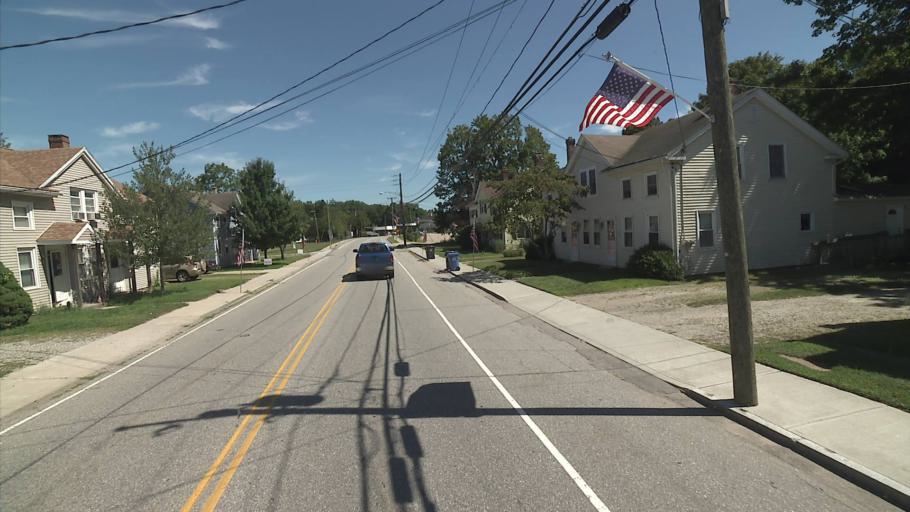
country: US
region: Connecticut
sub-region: New London County
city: Baltic
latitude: 41.6142
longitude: -72.0774
